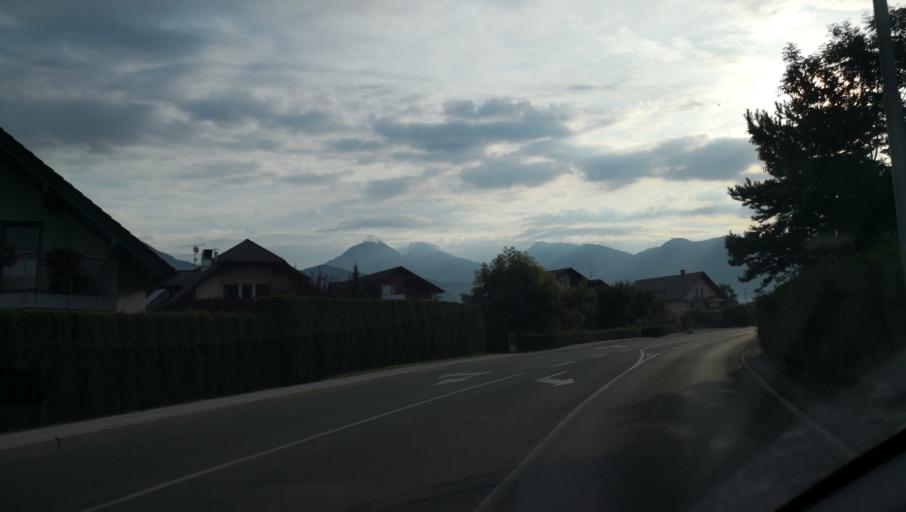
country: SI
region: Kranj
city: Britof
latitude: 46.2620
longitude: 14.3916
